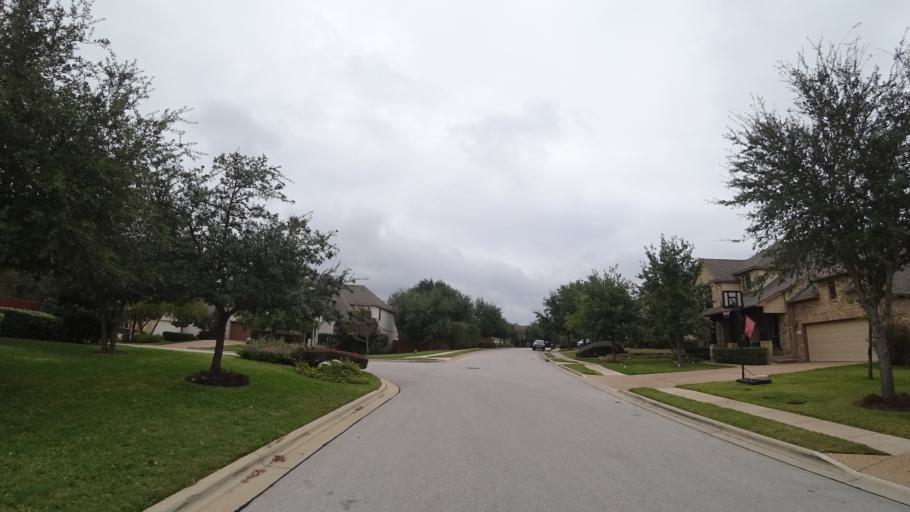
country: US
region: Texas
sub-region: Travis County
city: Hudson Bend
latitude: 30.3602
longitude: -97.9078
